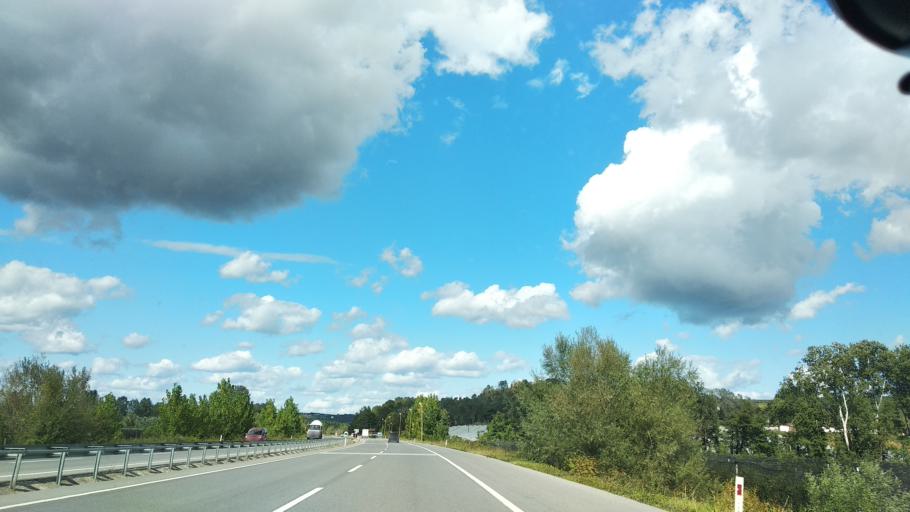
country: TR
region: Sakarya
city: Ortakoy
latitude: 41.0297
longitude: 30.6160
